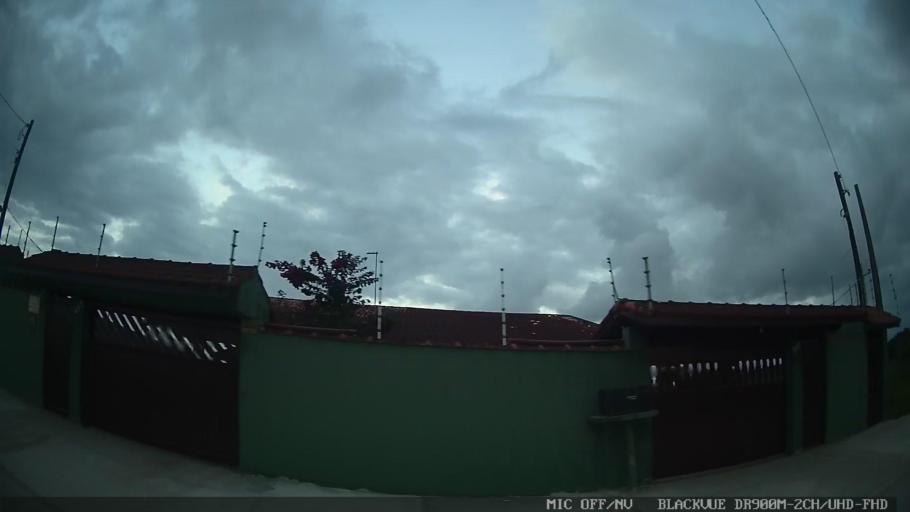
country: BR
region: Sao Paulo
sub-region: Itanhaem
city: Itanhaem
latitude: -24.1898
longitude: -46.8324
